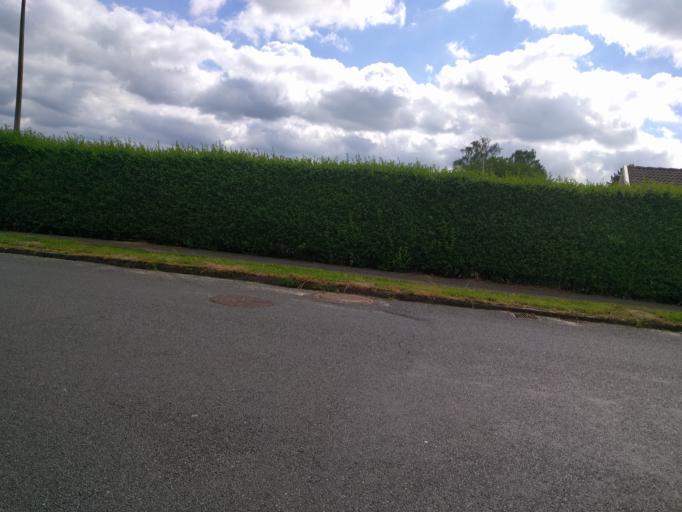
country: DK
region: South Denmark
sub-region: Kerteminde Kommune
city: Munkebo
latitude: 55.4481
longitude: 10.5462
